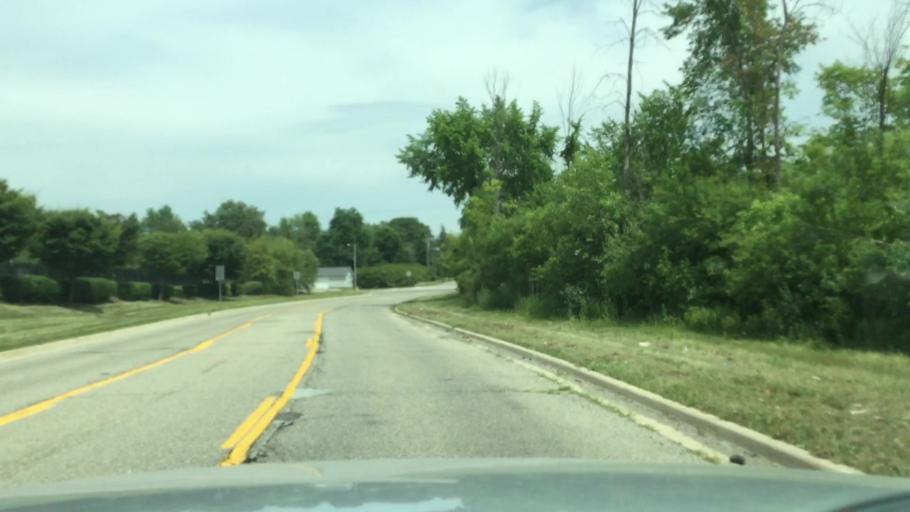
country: US
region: Michigan
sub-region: Genesee County
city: Flint
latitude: 42.9984
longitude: -83.7641
